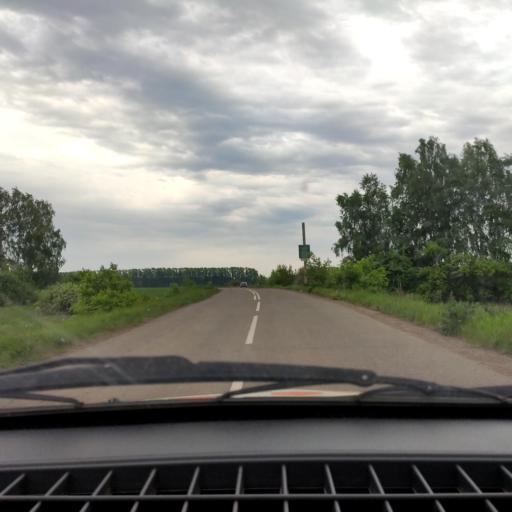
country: RU
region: Bashkortostan
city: Avdon
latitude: 54.5399
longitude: 55.7616
